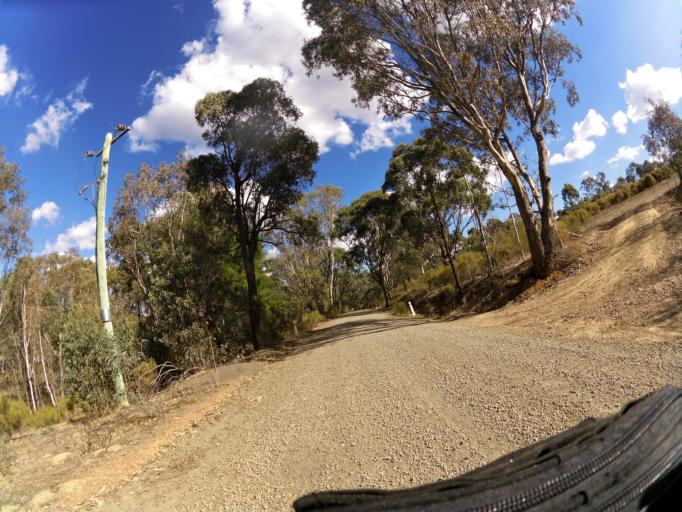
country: AU
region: Victoria
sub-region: Greater Bendigo
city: Kennington
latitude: -36.9597
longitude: 144.7798
